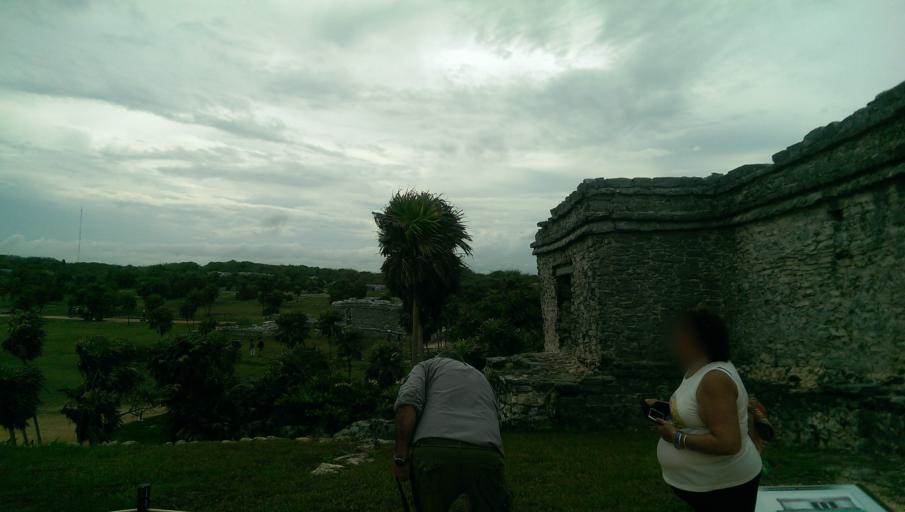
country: MX
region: Quintana Roo
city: Tulum
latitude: 20.2161
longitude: -87.4282
